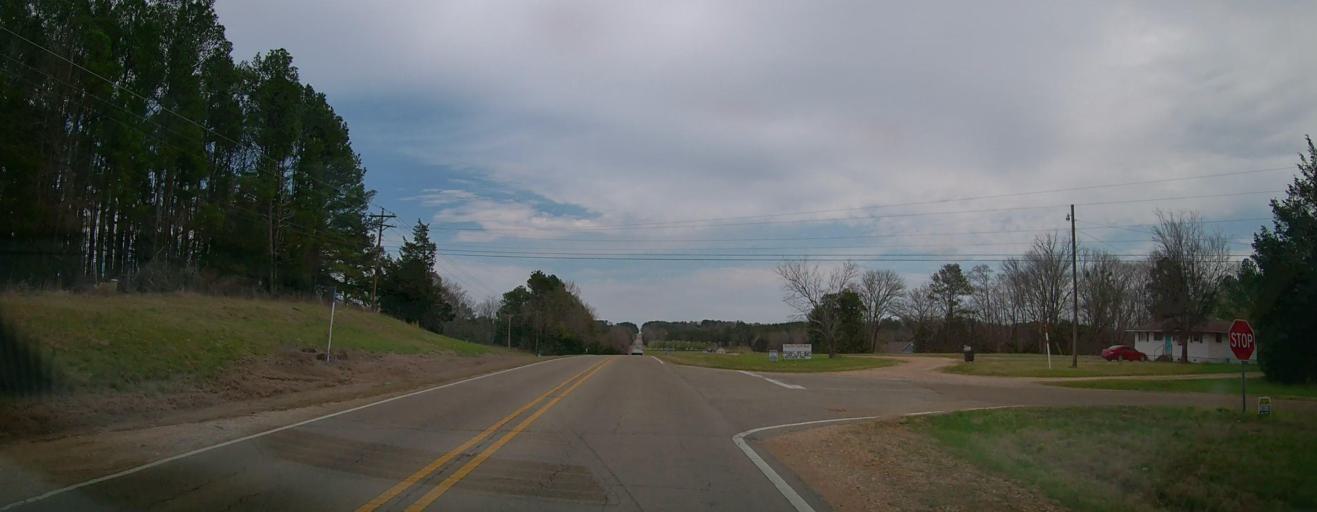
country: US
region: Mississippi
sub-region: Lee County
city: Plantersville
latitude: 34.2660
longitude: -88.6125
